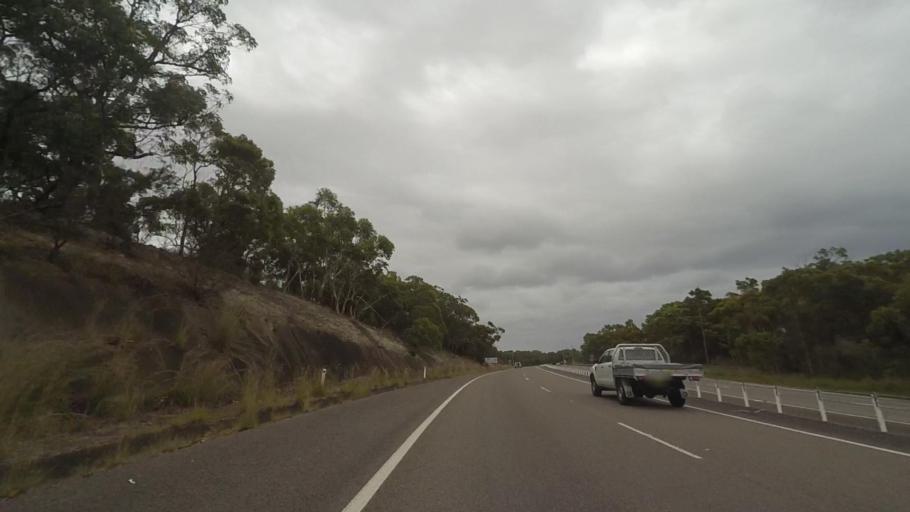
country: AU
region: New South Wales
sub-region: Wyong Shire
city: Kingfisher Shores
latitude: -33.1333
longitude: 151.6153
